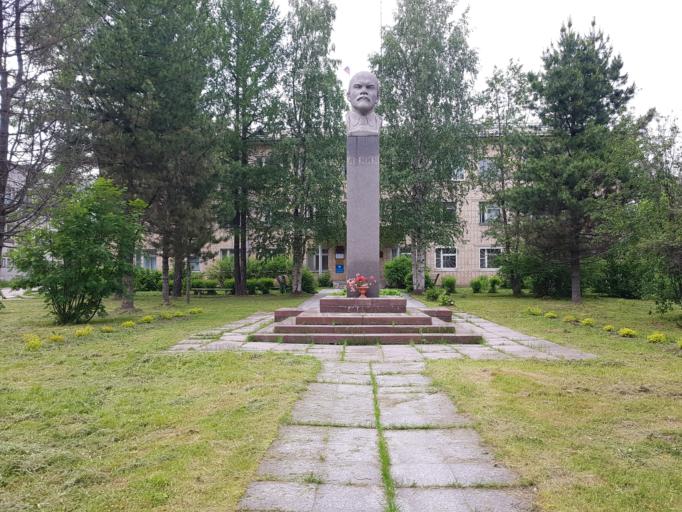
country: RU
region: Republic of Karelia
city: Kalevala
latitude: 65.1977
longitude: 31.1848
